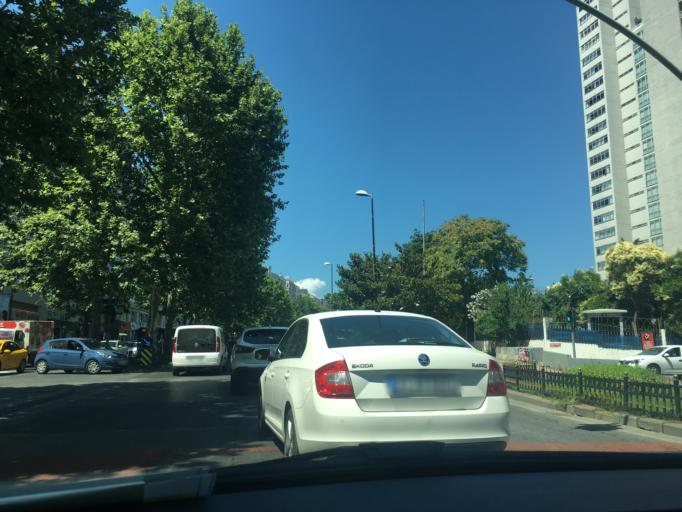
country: TR
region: Istanbul
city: Sisli
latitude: 41.0449
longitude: 28.9865
